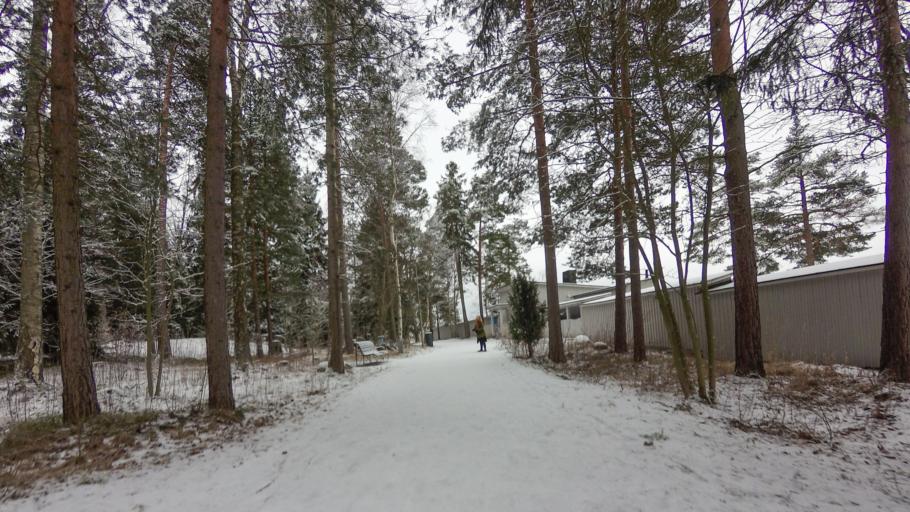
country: FI
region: Uusimaa
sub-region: Helsinki
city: Teekkarikylae
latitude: 60.1827
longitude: 24.8796
